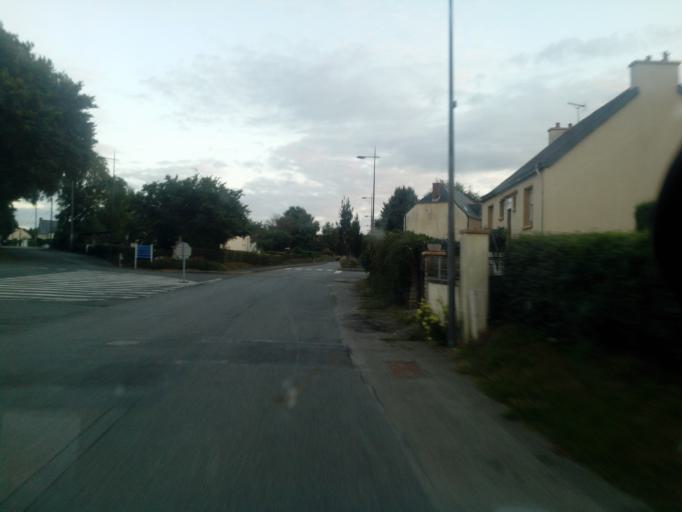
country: FR
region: Brittany
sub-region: Departement du Morbihan
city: Guegon
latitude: 47.9352
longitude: -2.5651
